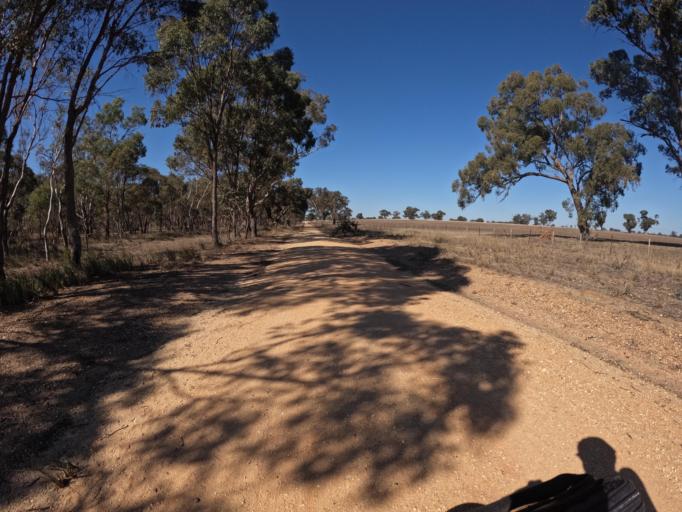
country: AU
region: Victoria
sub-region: Greater Bendigo
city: Kennington
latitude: -36.8325
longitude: 144.5936
